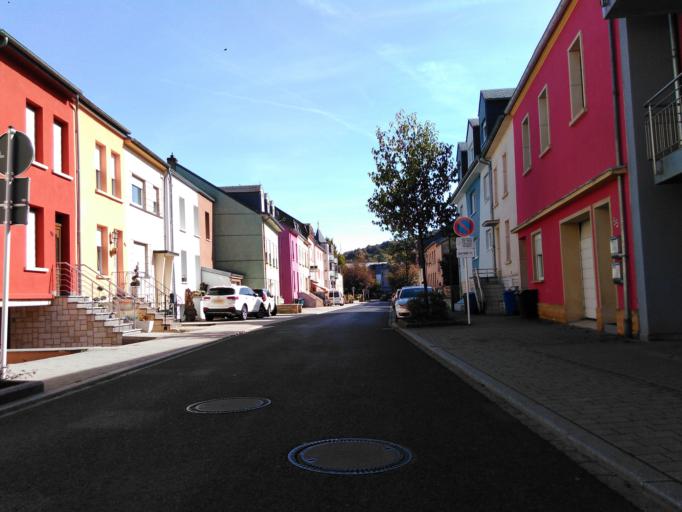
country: LU
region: Luxembourg
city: Tetange
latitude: 49.4742
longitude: 6.0357
